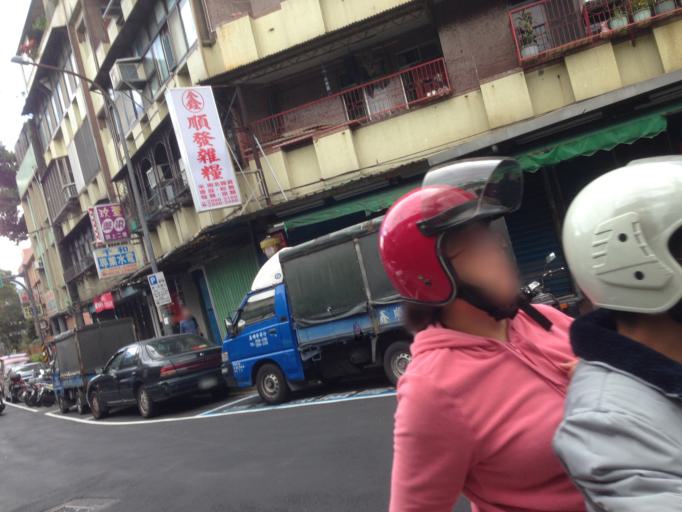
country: TW
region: Taipei
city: Taipei
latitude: 25.1335
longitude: 121.4982
